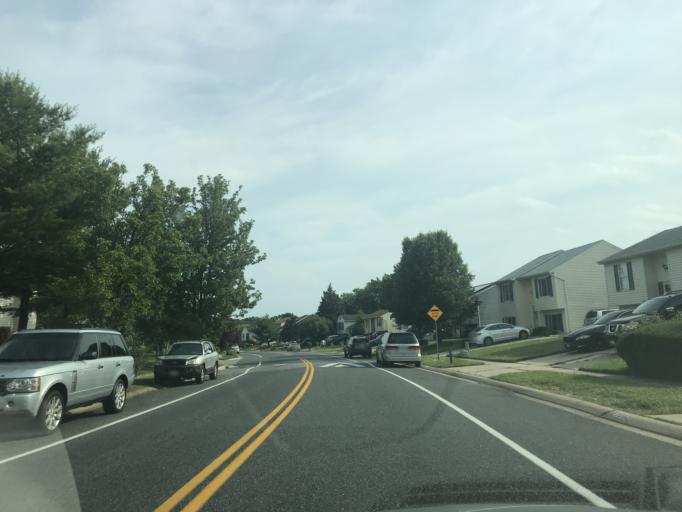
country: US
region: Maryland
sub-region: Harford County
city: Edgewood
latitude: 39.4249
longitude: -76.3227
